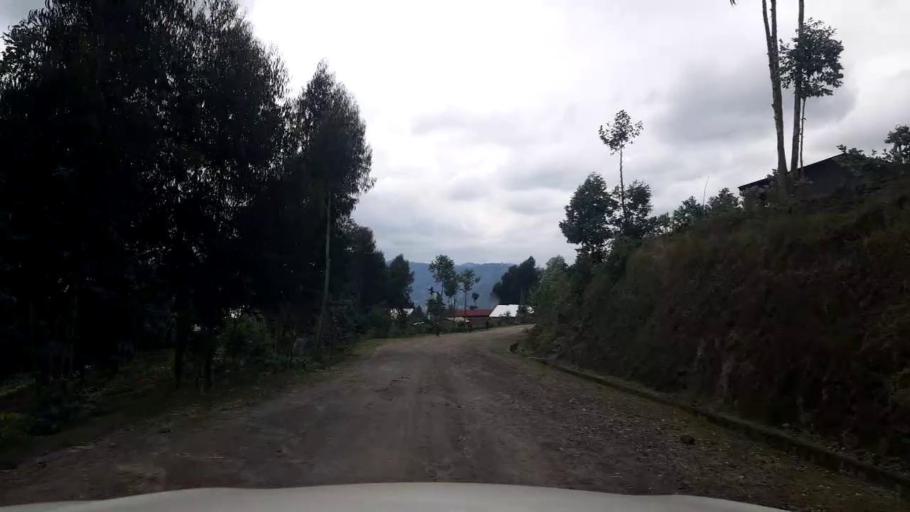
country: RW
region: Northern Province
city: Musanze
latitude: -1.5320
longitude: 29.5331
